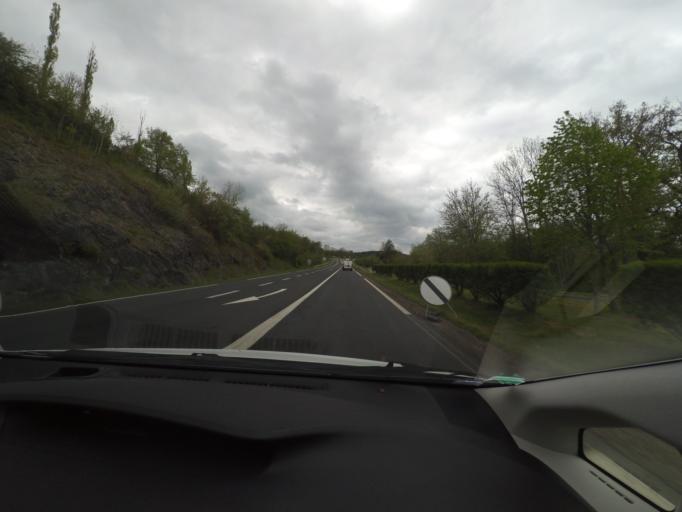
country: FR
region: Auvergne
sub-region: Departement du Puy-de-Dome
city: Gelles
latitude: 45.8604
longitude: 2.6722
